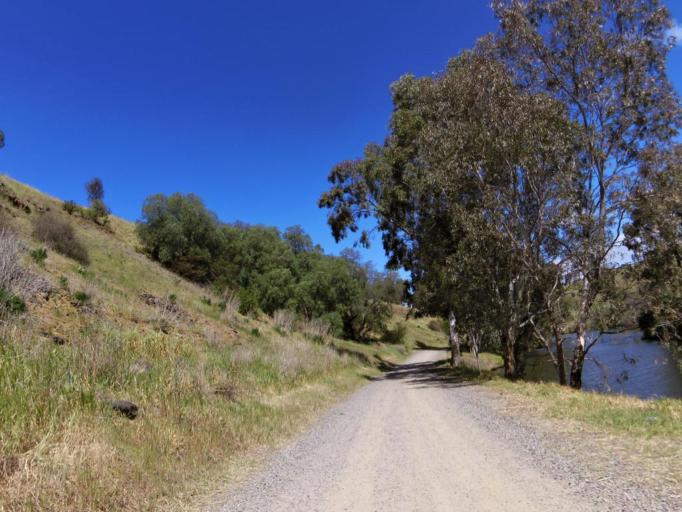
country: AU
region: Victoria
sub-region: Maribyrnong
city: Braybrook
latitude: -37.7667
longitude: 144.8536
